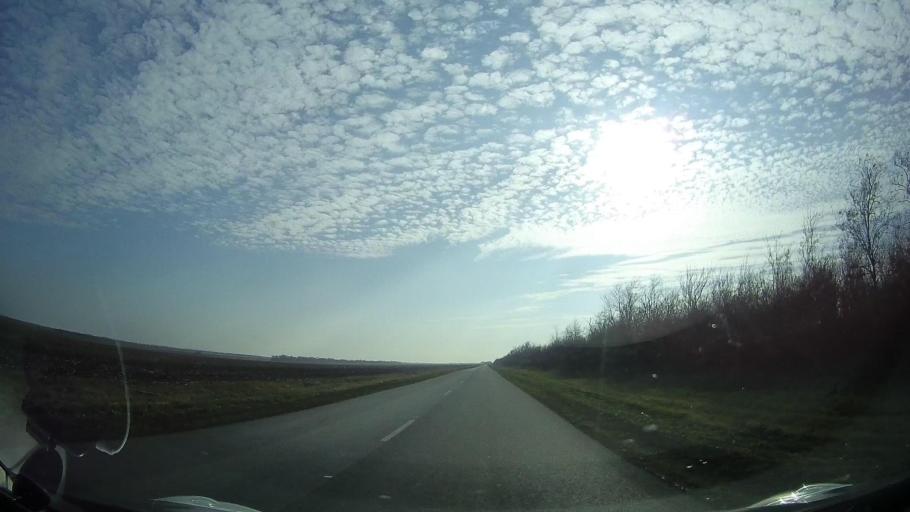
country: RU
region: Rostov
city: Veselyy
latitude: 46.9796
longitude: 40.7197
